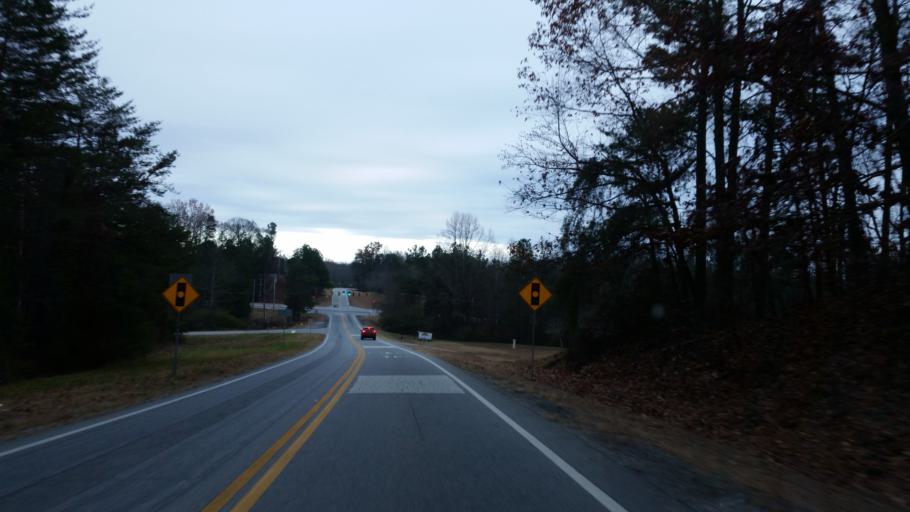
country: US
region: Georgia
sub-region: Dawson County
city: Dawsonville
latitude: 34.4010
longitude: -84.0133
